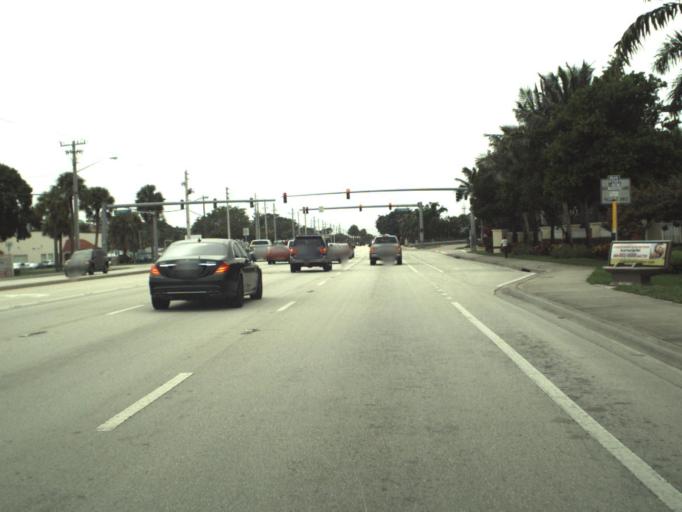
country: US
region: Florida
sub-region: Palm Beach County
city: Mangonia Park
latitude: 26.7746
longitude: -80.1078
